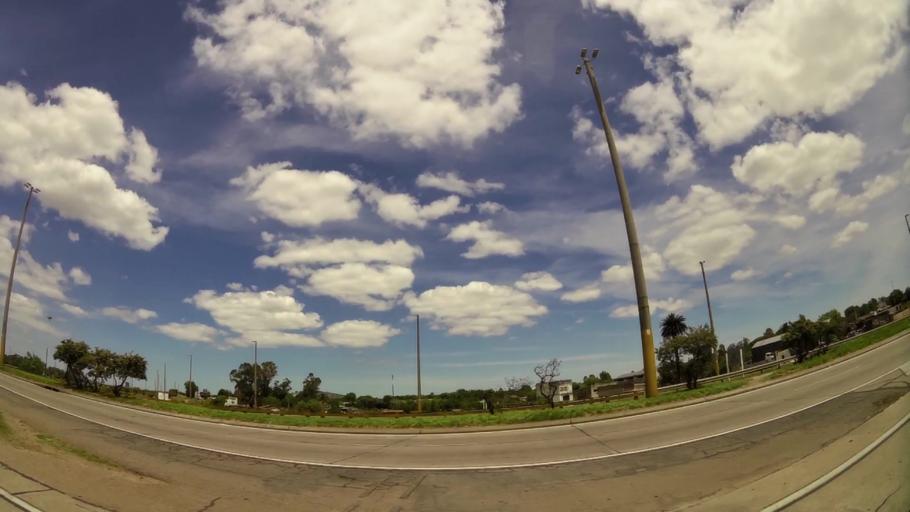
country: UY
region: Montevideo
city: Montevideo
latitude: -34.8562
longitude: -56.2583
